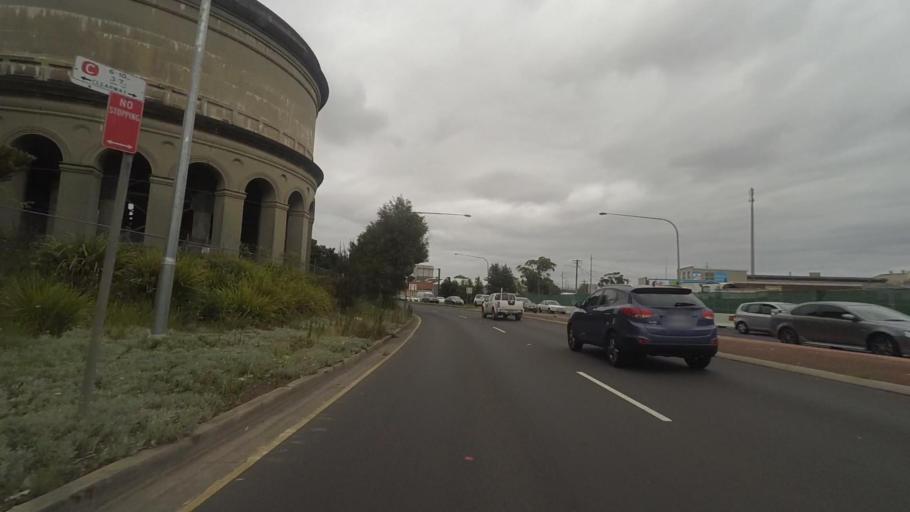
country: AU
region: New South Wales
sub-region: Bankstown
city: Bankstown
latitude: -33.9057
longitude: 151.0400
